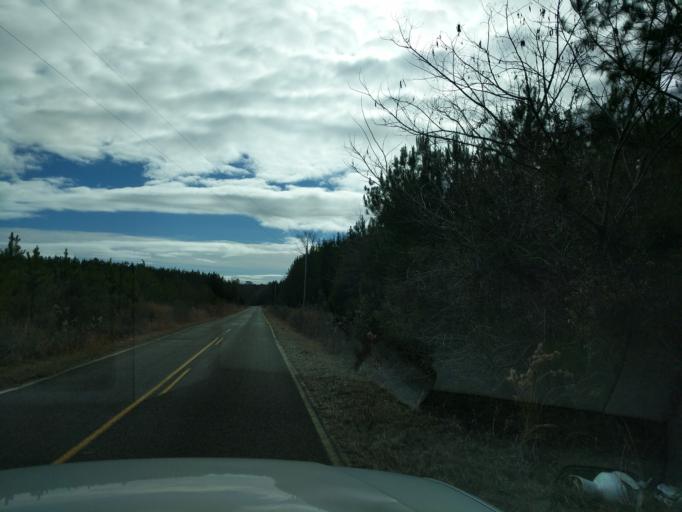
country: US
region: South Carolina
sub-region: Edgefield County
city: Edgefield
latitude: 33.9171
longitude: -82.0067
